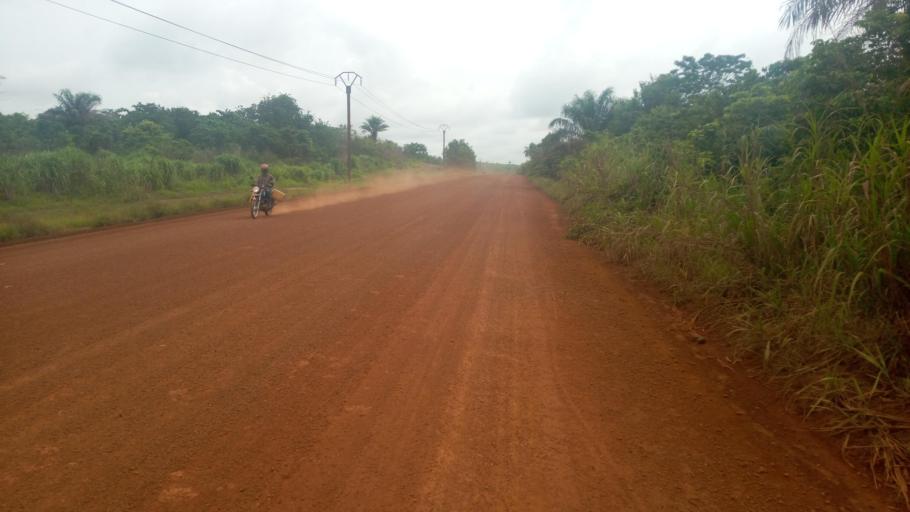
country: SL
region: Southern Province
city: Mogbwemo
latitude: 7.7166
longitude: -12.2853
